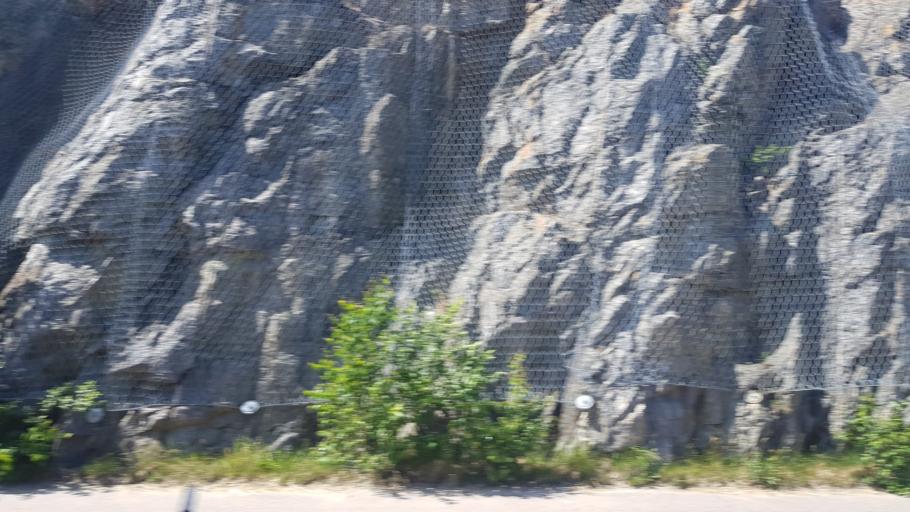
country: SE
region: Vaestra Goetaland
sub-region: Tjorns Kommun
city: Skaerhamn
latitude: 57.9669
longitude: 11.5565
